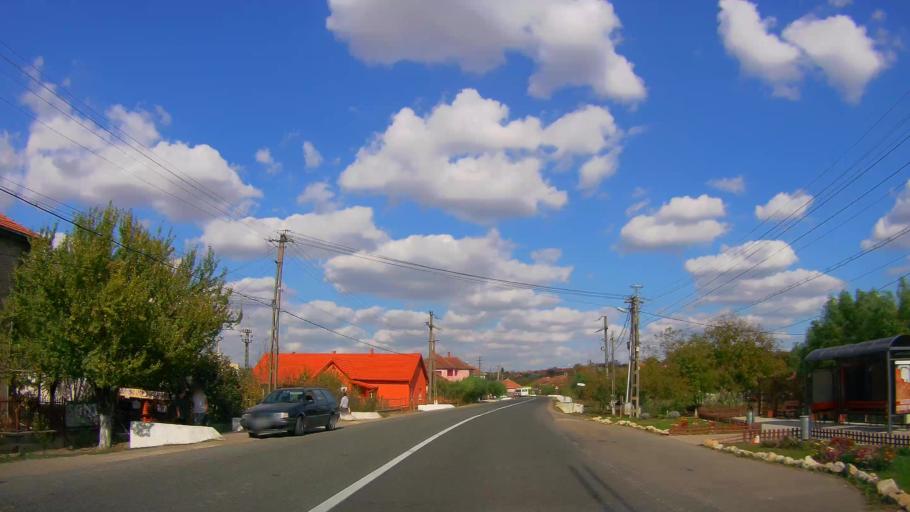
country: RO
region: Satu Mare
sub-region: Oras Ardud
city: Ardud
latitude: 47.6316
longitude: 22.8827
